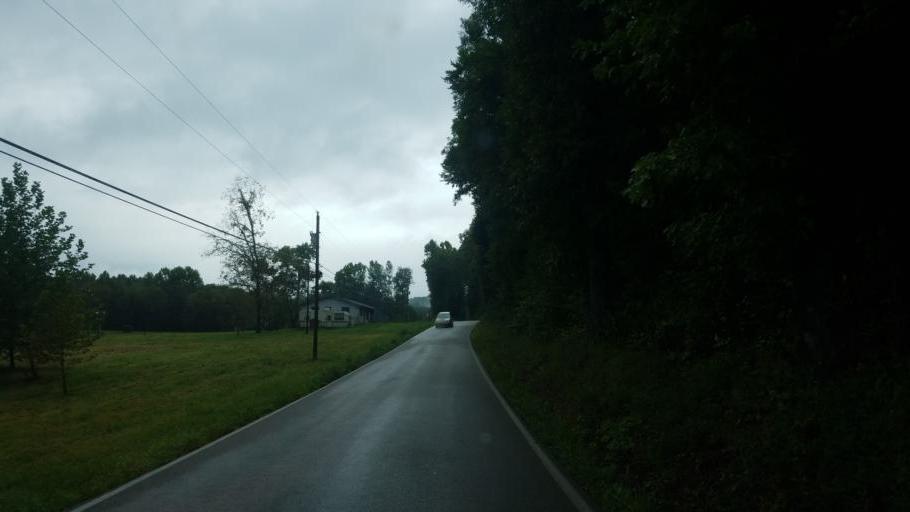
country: US
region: Kentucky
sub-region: Rowan County
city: Morehead
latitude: 38.1701
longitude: -83.4968
